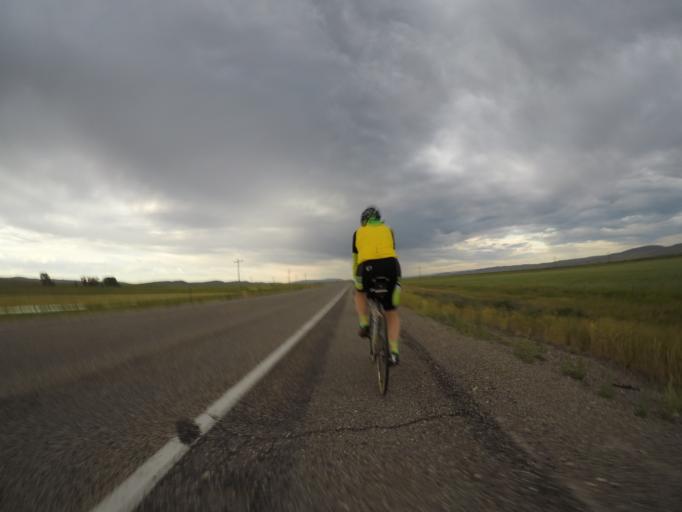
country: US
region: Utah
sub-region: Rich County
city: Randolph
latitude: 41.9491
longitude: -110.9517
